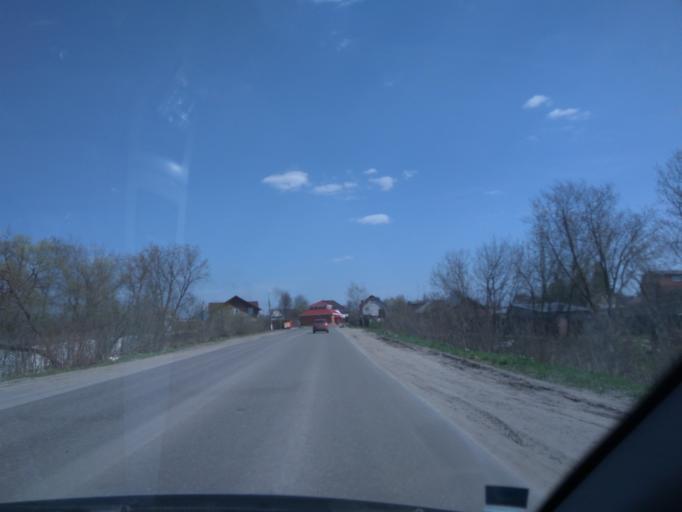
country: RU
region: Moskovskaya
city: Ramenskoye
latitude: 55.5573
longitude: 38.2271
